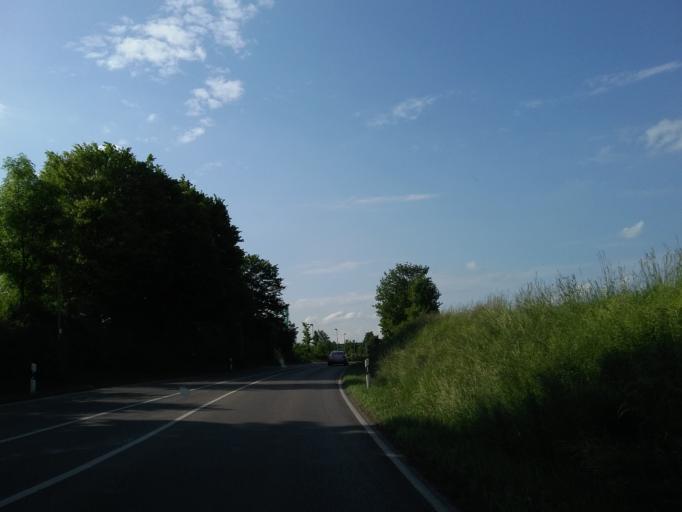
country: DE
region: Baden-Wuerttemberg
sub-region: Regierungsbezirk Stuttgart
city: Backnang
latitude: 48.9310
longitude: 9.4472
